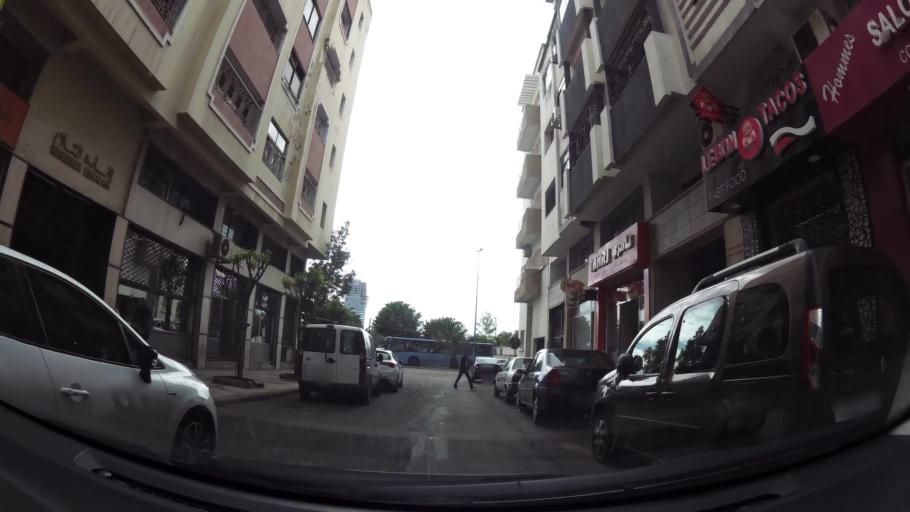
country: MA
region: Grand Casablanca
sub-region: Casablanca
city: Casablanca
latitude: 33.5654
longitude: -7.6683
